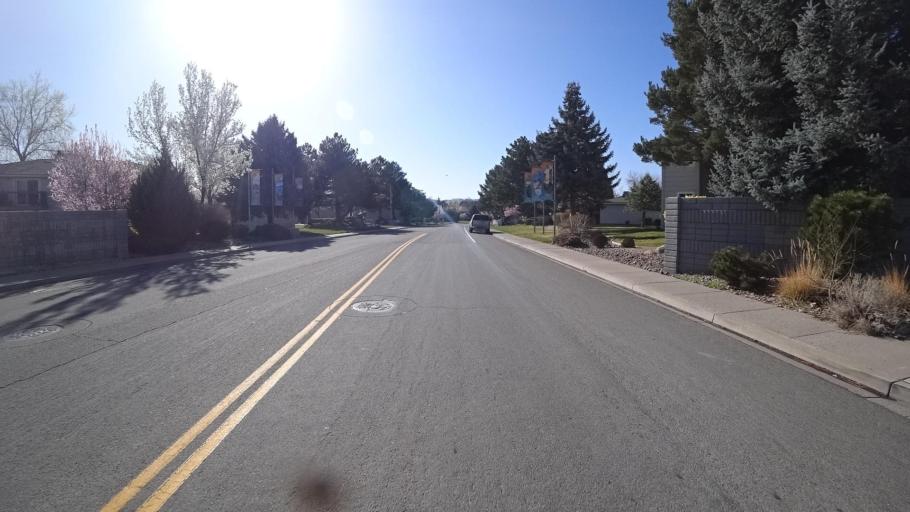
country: US
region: Nevada
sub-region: Washoe County
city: Sparks
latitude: 39.4569
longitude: -119.7757
